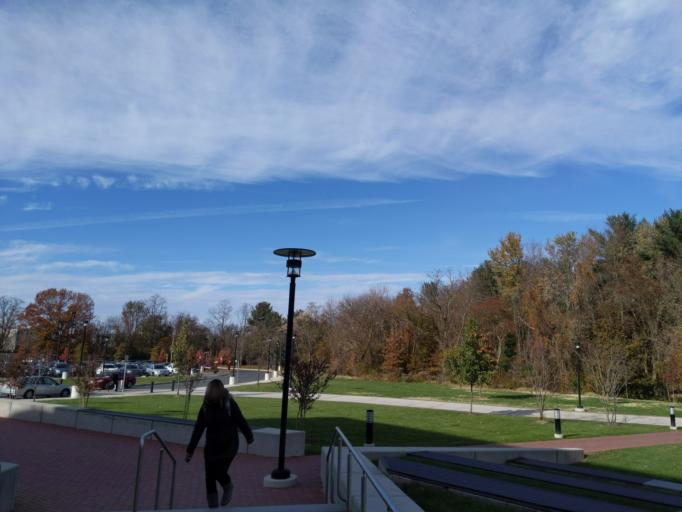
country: US
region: New Jersey
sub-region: Gloucester County
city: Glassboro
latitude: 39.7103
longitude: -75.1228
